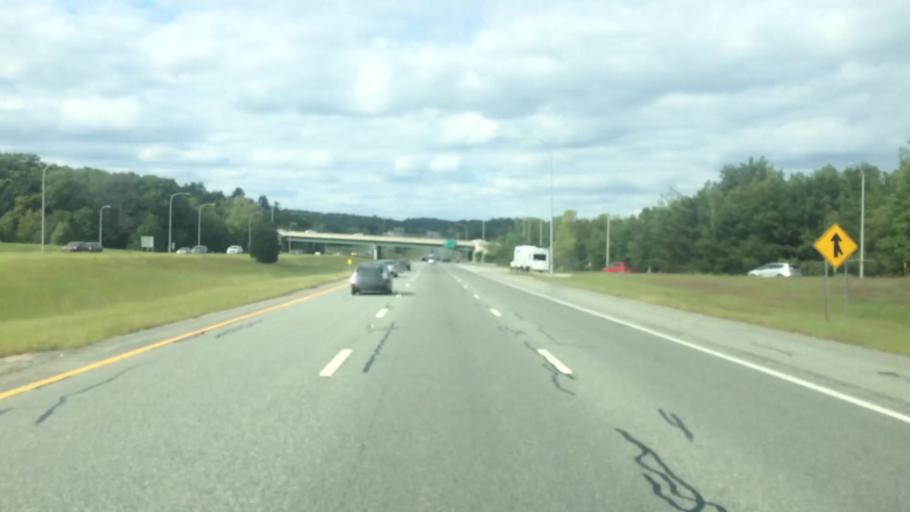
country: US
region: Rhode Island
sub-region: Providence County
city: Greenville
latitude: 41.8664
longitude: -71.5146
